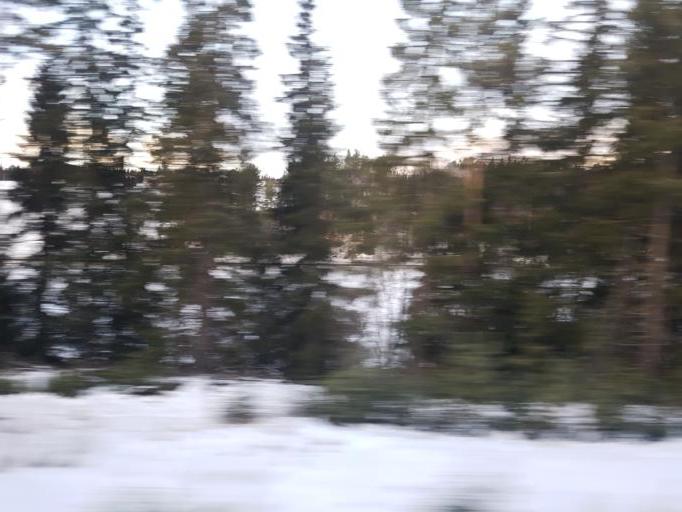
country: NO
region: Sor-Trondelag
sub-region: Rennebu
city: Berkak
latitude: 62.8891
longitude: 10.1027
